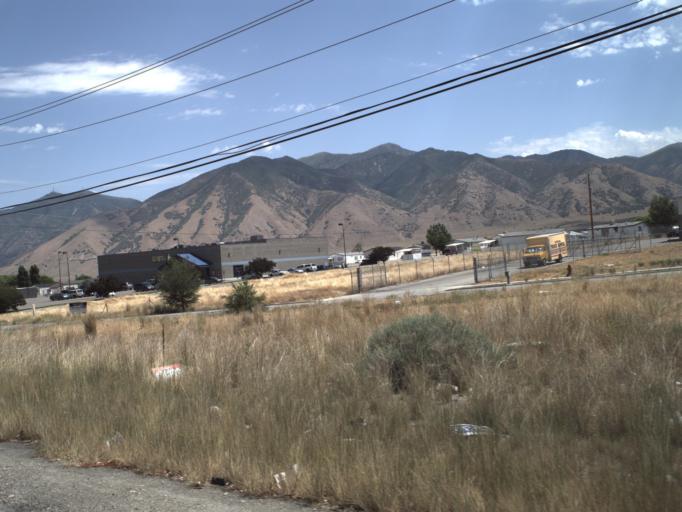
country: US
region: Utah
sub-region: Tooele County
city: Tooele
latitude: 40.5550
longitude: -112.2974
